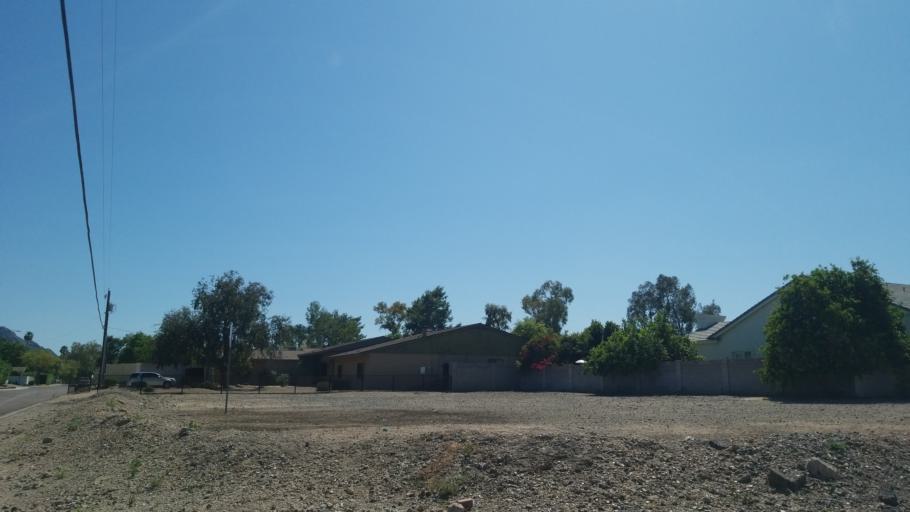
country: US
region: Arizona
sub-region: Maricopa County
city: Paradise Valley
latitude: 33.5920
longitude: -112.0273
